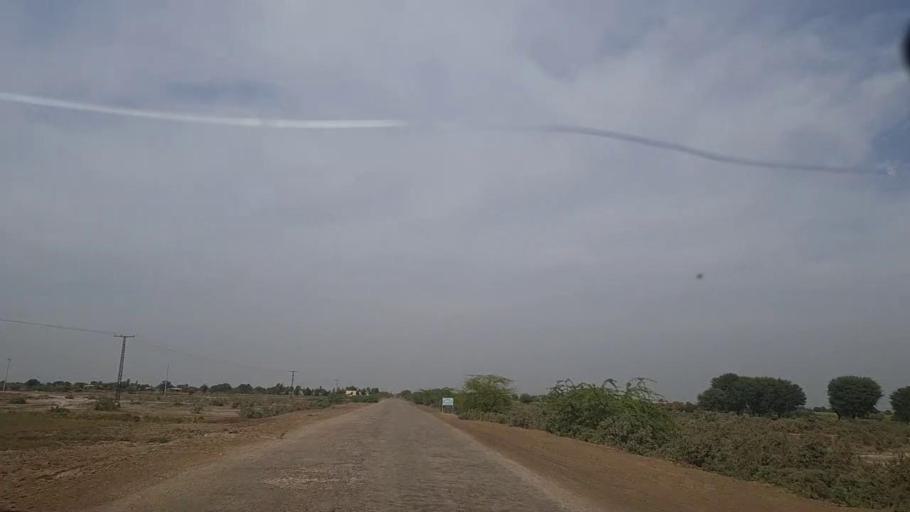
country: PK
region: Sindh
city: Pithoro
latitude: 25.5599
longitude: 69.3629
